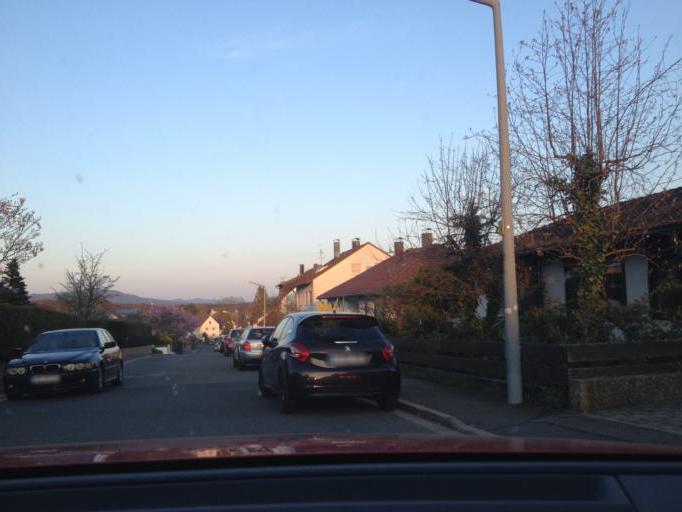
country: DE
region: Bavaria
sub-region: Regierungsbezirk Mittelfranken
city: Lauf an der Pegnitz
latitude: 49.5203
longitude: 11.2834
